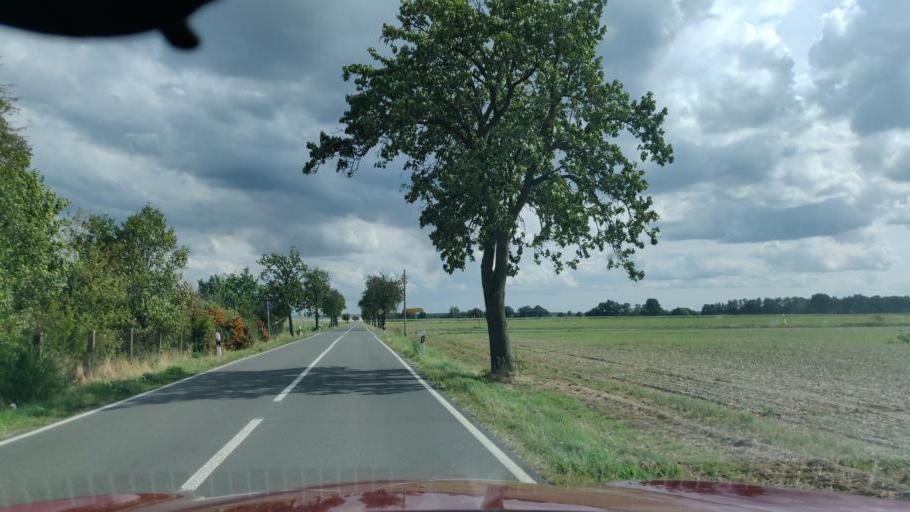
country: DE
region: Saxony
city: Schildau
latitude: 51.4829
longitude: 12.9210
